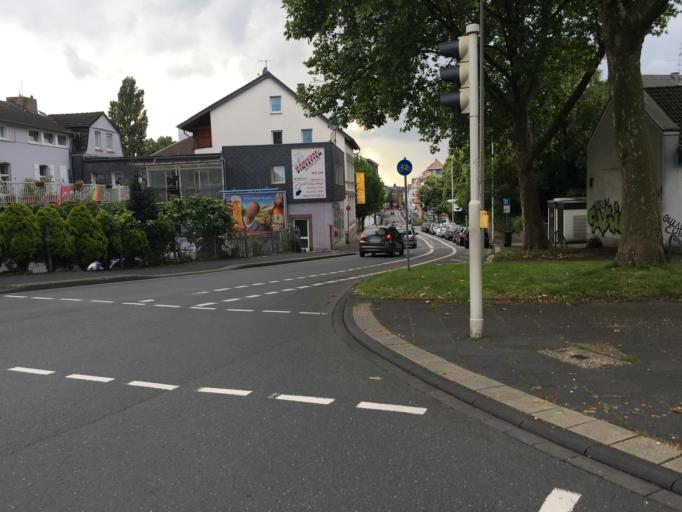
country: DE
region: North Rhine-Westphalia
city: Haan
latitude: 51.1594
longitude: 7.0018
